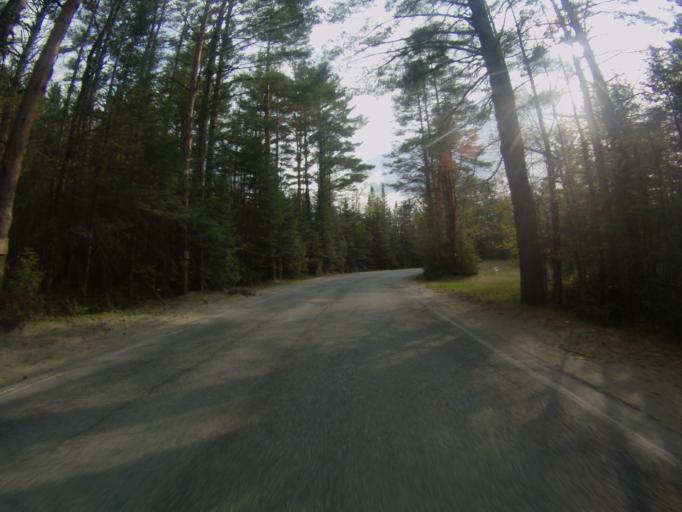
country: US
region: New York
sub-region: Warren County
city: Warrensburg
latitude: 43.8430
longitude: -73.8275
